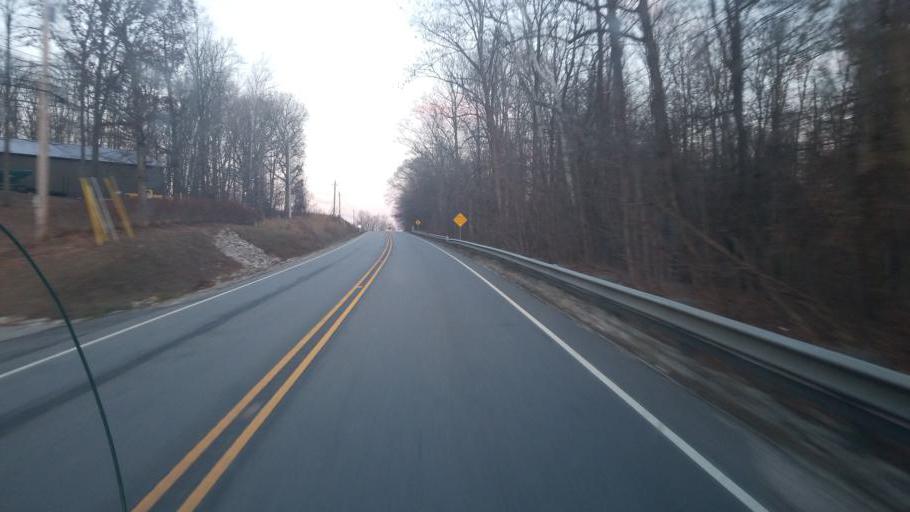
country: US
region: Indiana
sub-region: Lawrence County
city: Bedford
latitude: 38.8750
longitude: -86.3168
